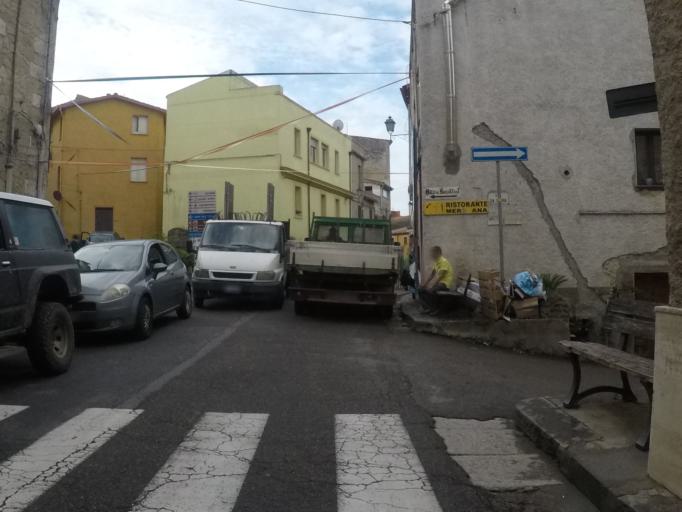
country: IT
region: Sardinia
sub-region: Provincia di Oristano
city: Cuglieri
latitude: 40.1886
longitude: 8.5675
